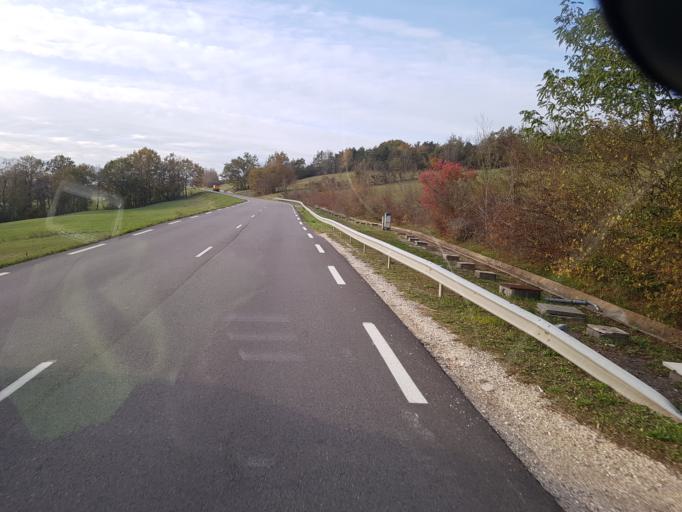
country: FR
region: Rhone-Alpes
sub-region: Departement de la Haute-Savoie
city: Frangy
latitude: 46.0522
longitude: 5.8799
